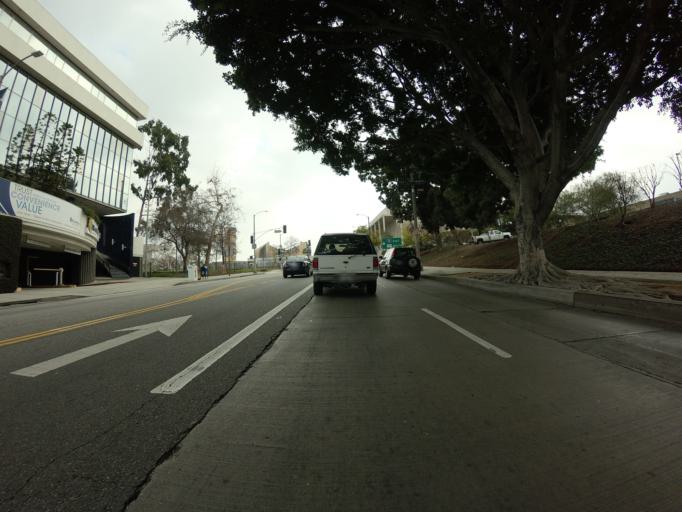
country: US
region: California
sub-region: Los Angeles County
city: Los Angeles
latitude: 34.0596
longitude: -118.2481
